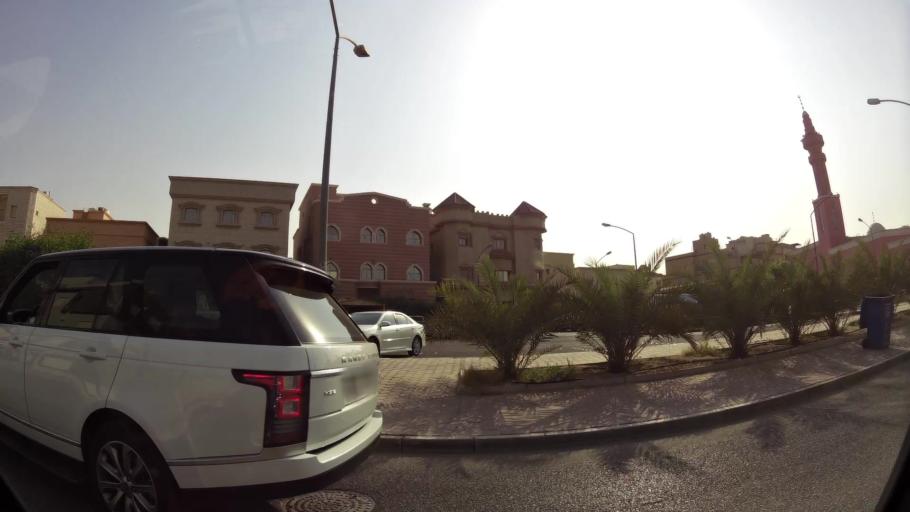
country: KW
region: Al Asimah
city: Ar Rabiyah
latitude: 29.3013
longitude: 47.8078
